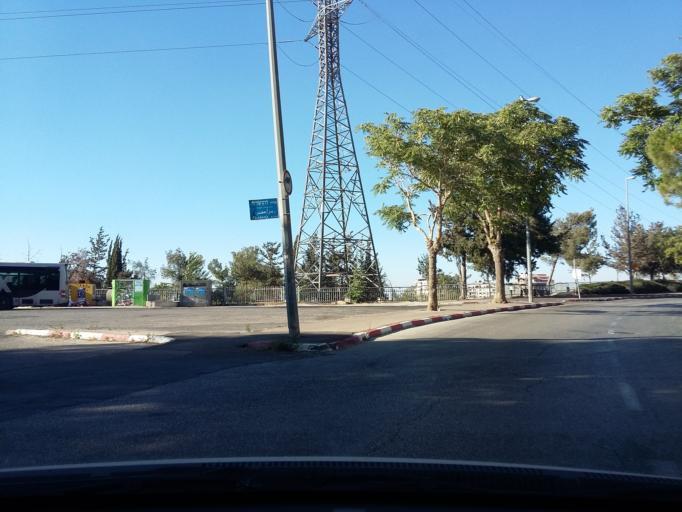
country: PS
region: West Bank
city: `Anata
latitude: 31.8071
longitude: 35.2377
